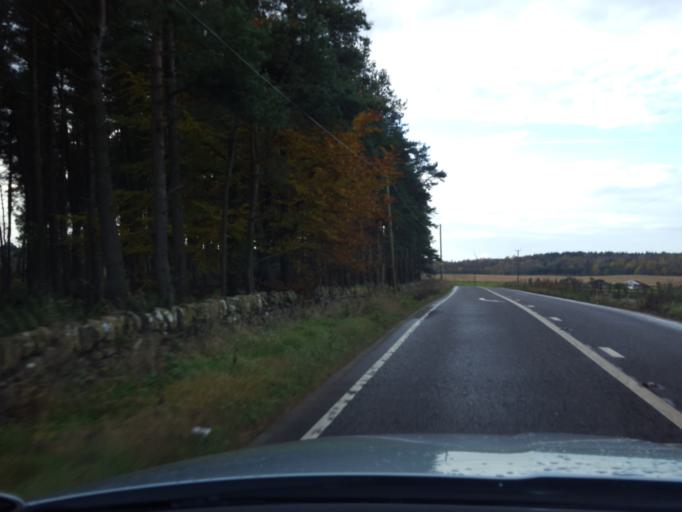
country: GB
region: Scotland
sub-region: South Lanarkshire
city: Carnwath
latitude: 55.7162
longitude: -3.5895
